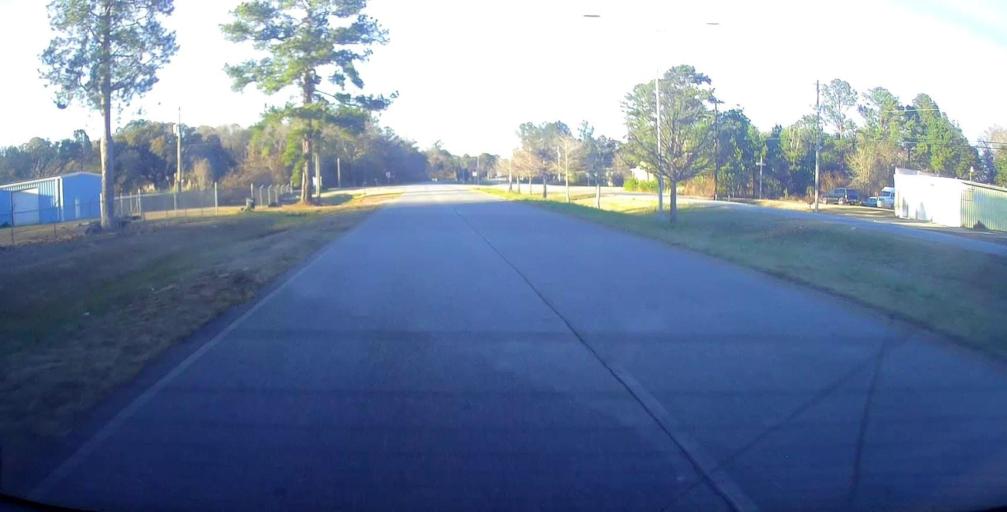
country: US
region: Georgia
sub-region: Dougherty County
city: Albany
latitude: 31.5546
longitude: -84.2250
